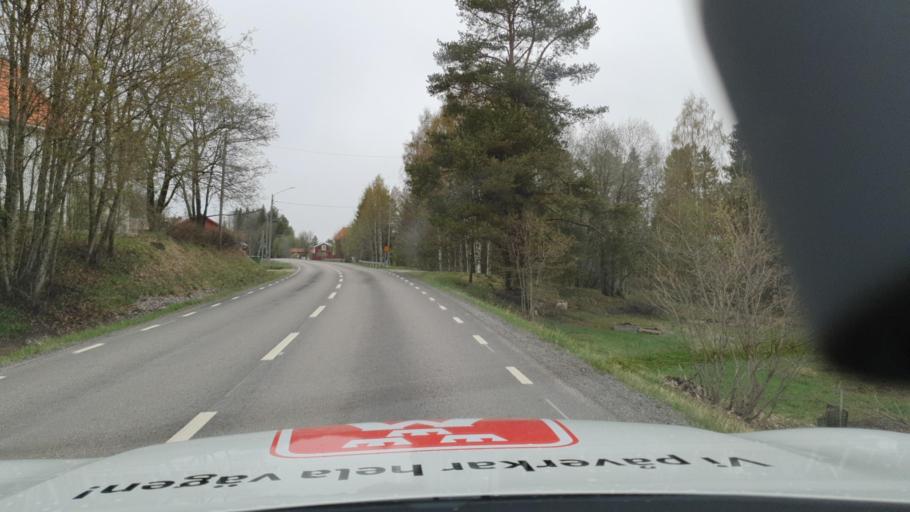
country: SE
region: Vaesterbotten
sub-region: Vannas Kommun
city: Vaennaes
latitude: 63.7831
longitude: 19.8403
